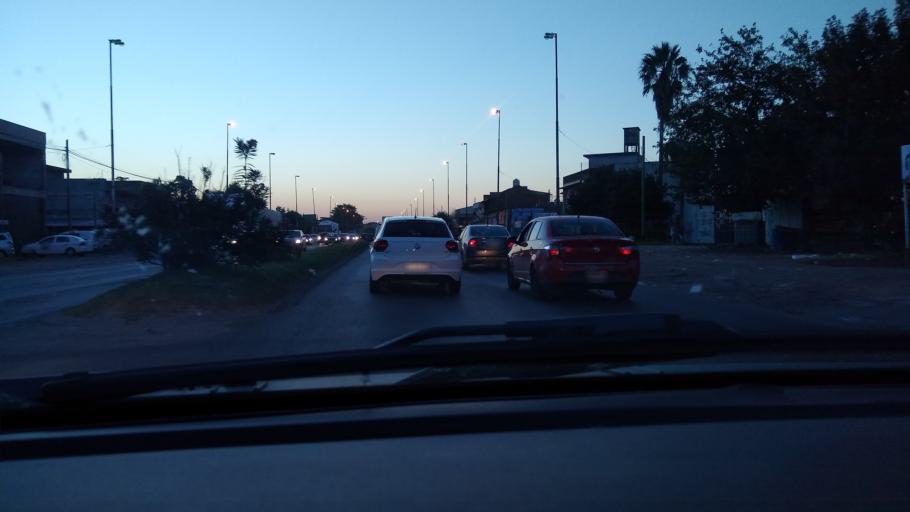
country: AR
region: Buenos Aires
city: San Justo
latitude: -34.6812
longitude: -58.5776
